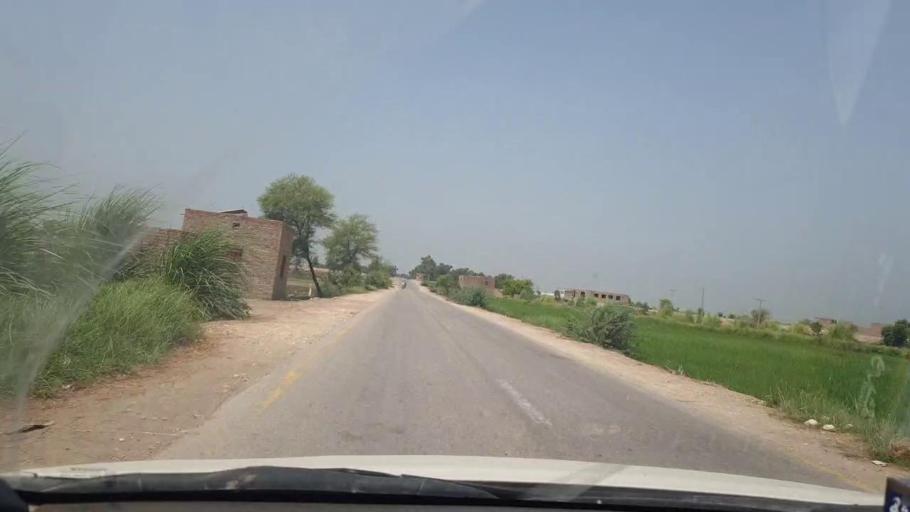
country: PK
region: Sindh
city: Shikarpur
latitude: 27.9543
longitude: 68.6678
